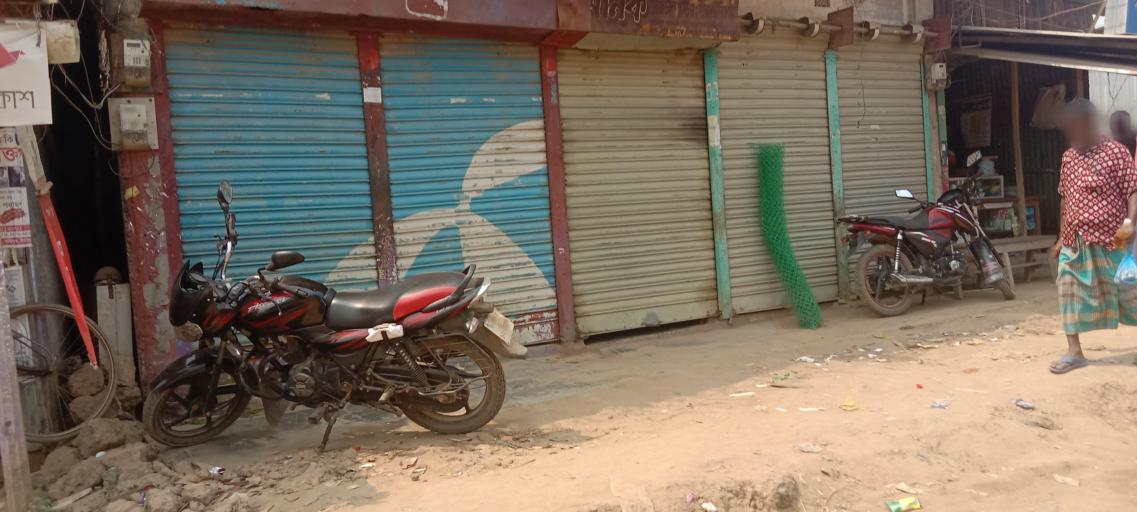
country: BD
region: Dhaka
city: Sakhipur
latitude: 24.3071
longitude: 90.2700
